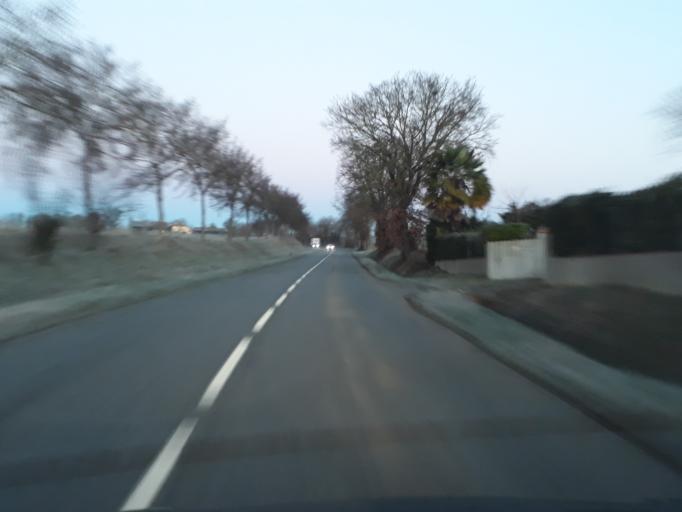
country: FR
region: Midi-Pyrenees
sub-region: Departement du Gers
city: Samatan
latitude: 43.4957
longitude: 0.9202
